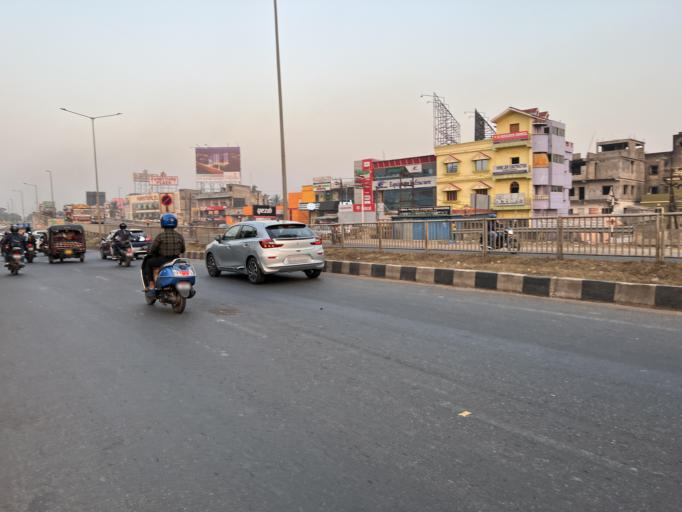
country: IN
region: Odisha
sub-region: Khordha
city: Bhubaneshwar
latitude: 20.3071
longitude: 85.8699
